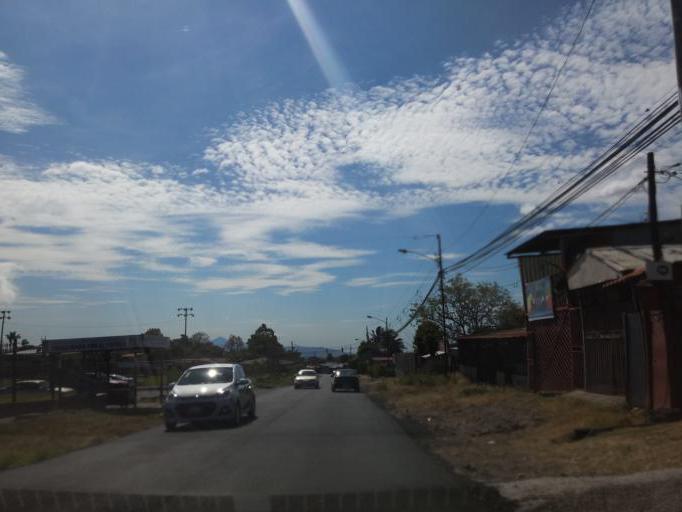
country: CR
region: Heredia
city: Llorente
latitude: 10.0297
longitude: -84.1707
